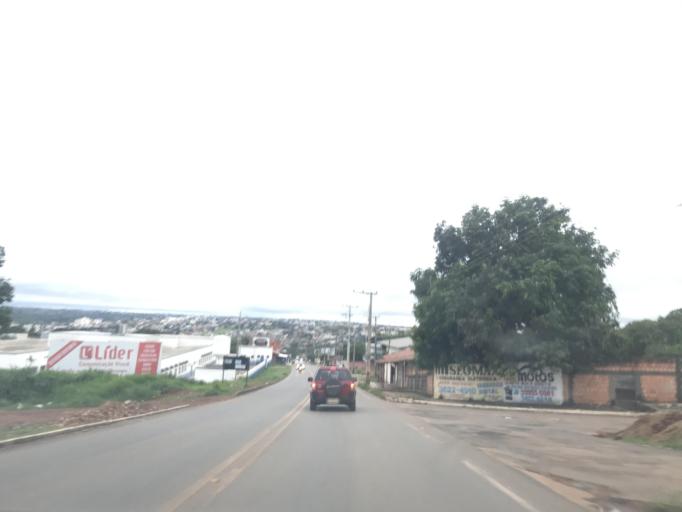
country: BR
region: Goias
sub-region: Luziania
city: Luziania
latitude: -16.2636
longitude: -47.9619
